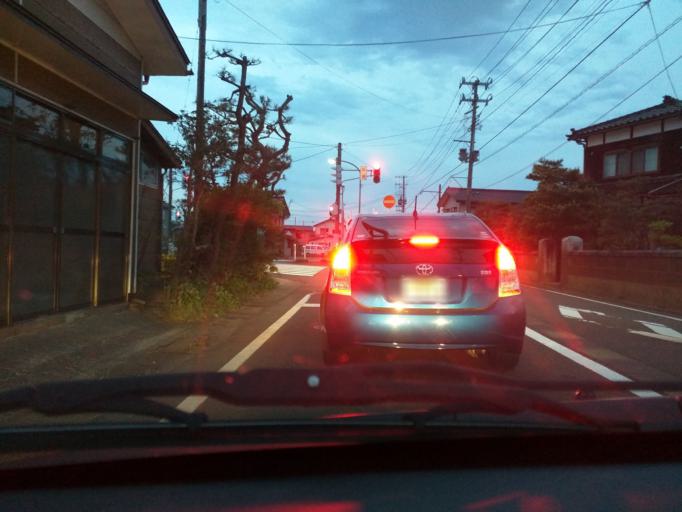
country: JP
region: Niigata
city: Kashiwazaki
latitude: 37.3379
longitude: 138.6172
